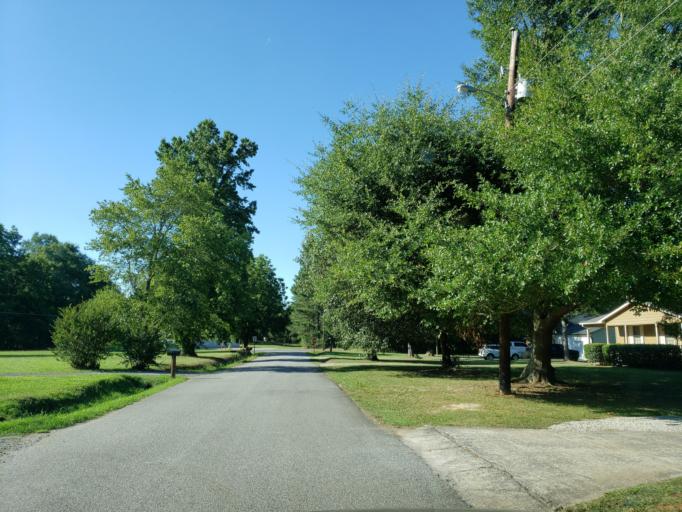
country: US
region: Georgia
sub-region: Bartow County
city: Cartersville
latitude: 34.1178
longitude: -84.8560
